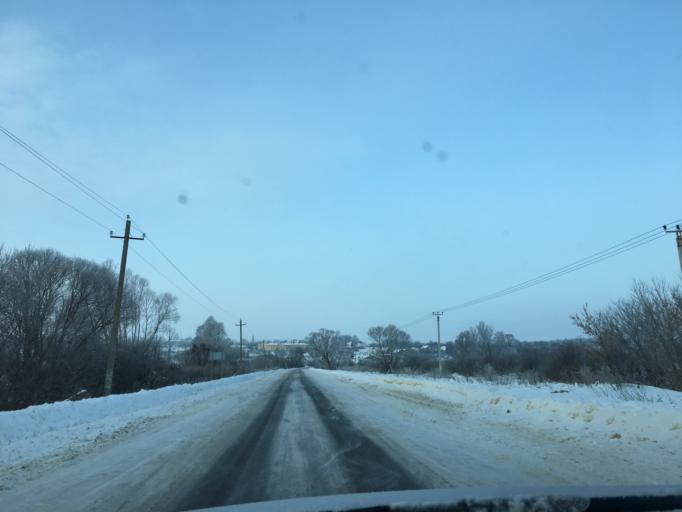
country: RU
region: Belgorod
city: Severnyy
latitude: 50.7272
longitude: 36.6098
